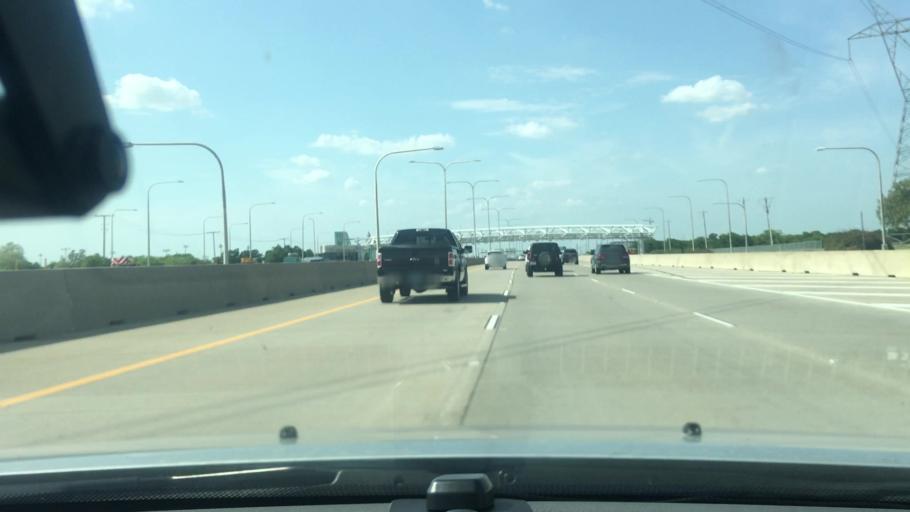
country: US
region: Texas
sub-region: Collin County
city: Frisco
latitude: 33.1615
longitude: -96.8399
